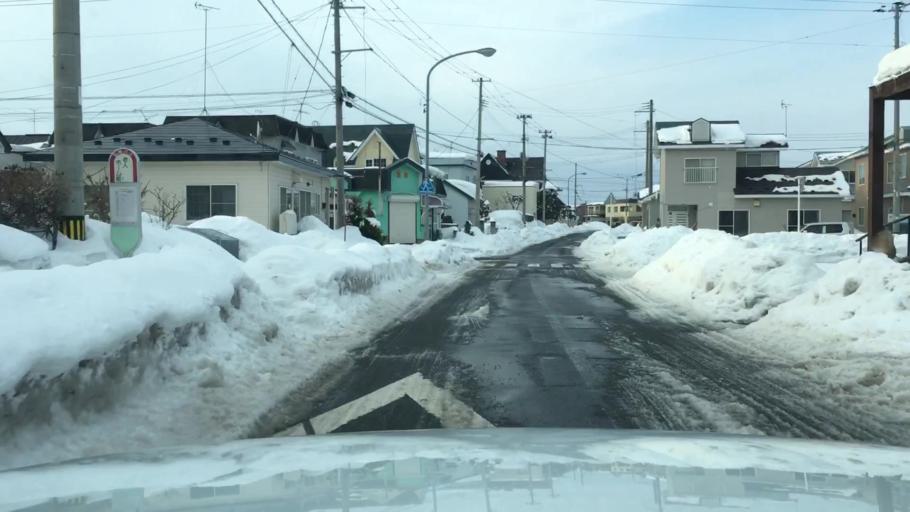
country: JP
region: Aomori
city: Hirosaki
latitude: 40.5774
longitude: 140.4893
